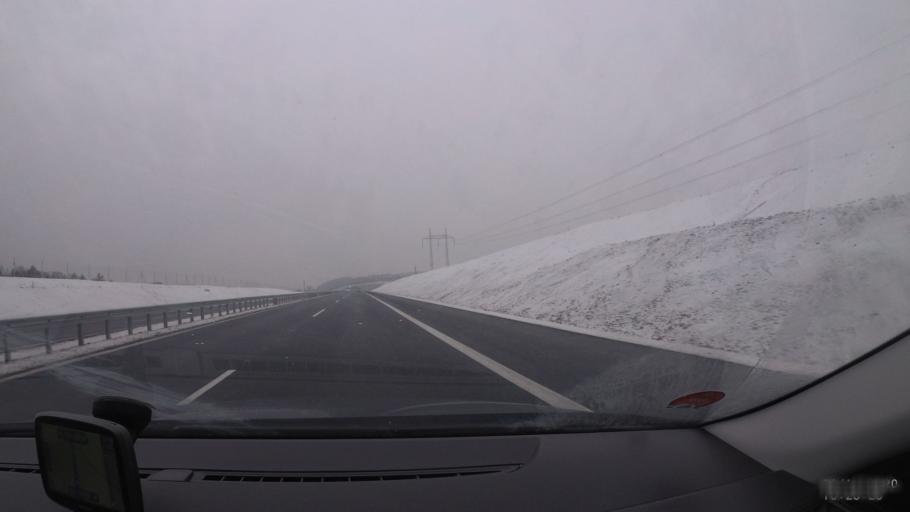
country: CZ
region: Central Bohemia
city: Revnicov
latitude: 50.1778
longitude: 13.7923
